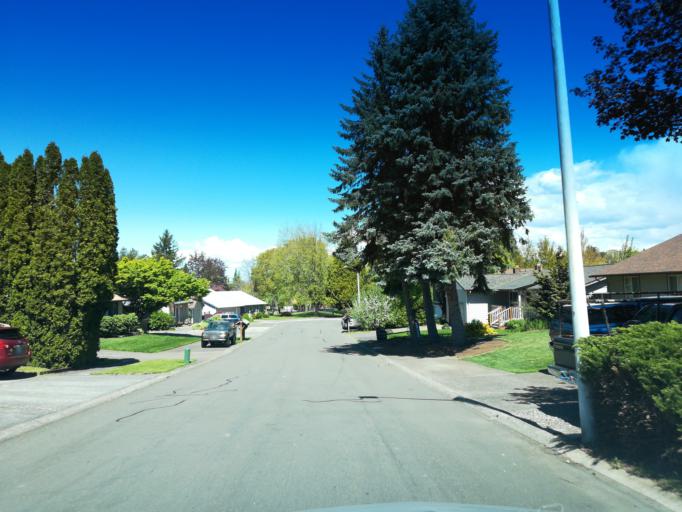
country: US
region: Oregon
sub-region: Multnomah County
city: Troutdale
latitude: 45.5140
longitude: -122.3854
